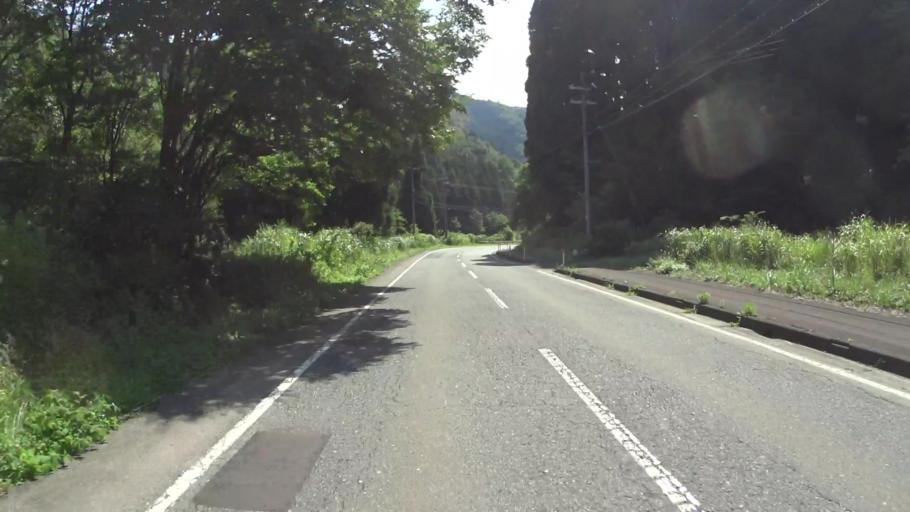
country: JP
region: Fukui
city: Obama
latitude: 35.3963
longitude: 135.5997
